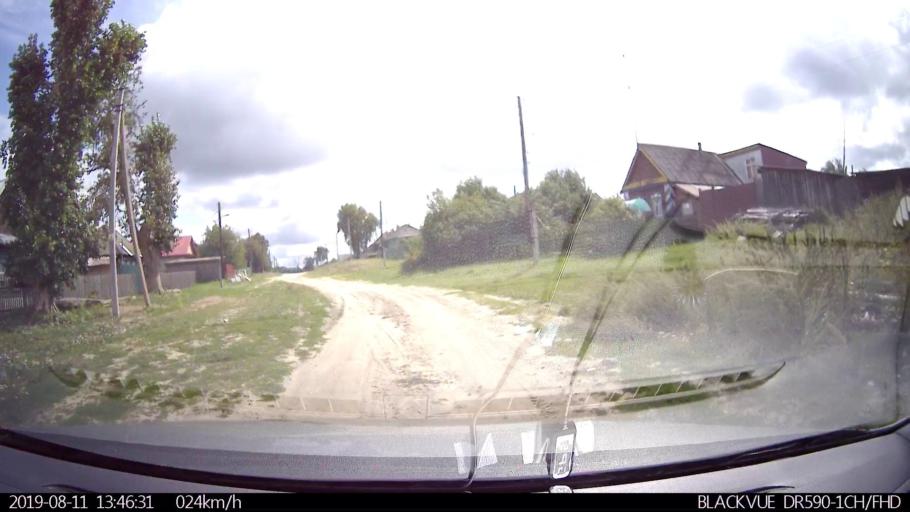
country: RU
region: Ulyanovsk
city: Ignatovka
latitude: 53.8506
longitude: 47.5756
